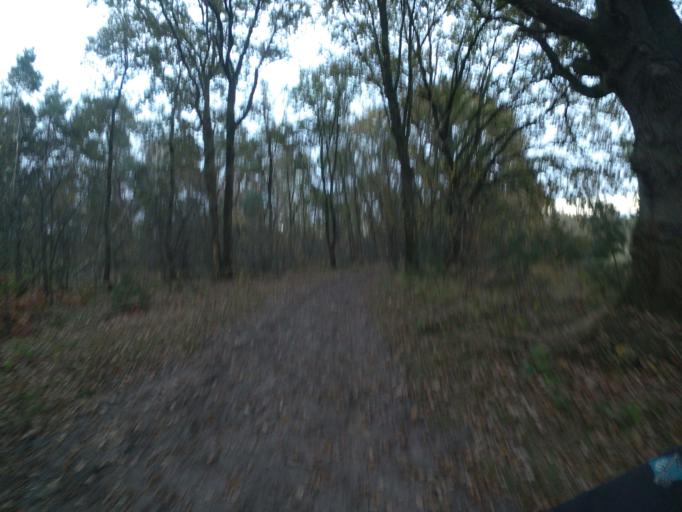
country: NL
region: North Brabant
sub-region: Gemeente Haaren
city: Haaren
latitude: 51.6512
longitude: 5.1961
